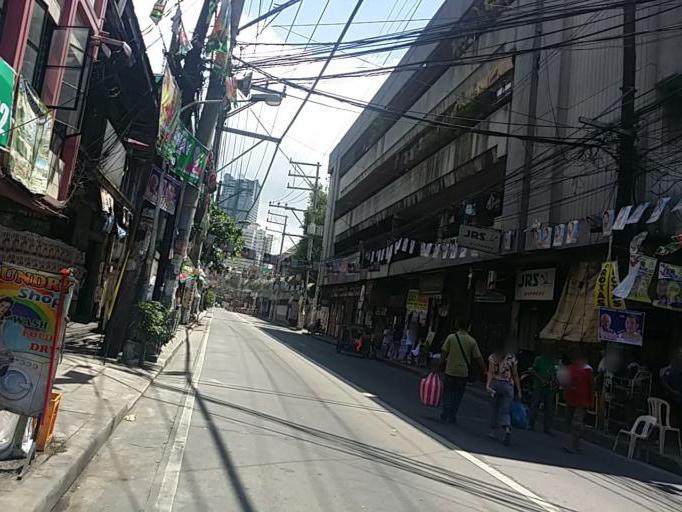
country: PH
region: Metro Manila
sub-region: City of Manila
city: Quiapo
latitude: 14.6021
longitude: 120.9884
